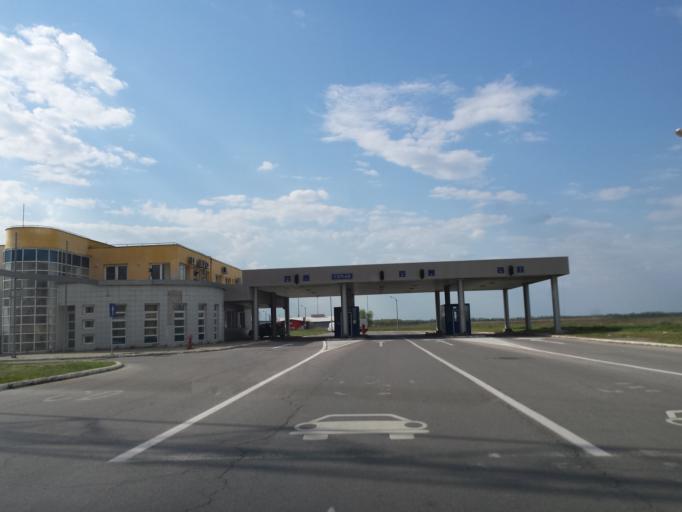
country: HU
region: Csongrad
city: Kiszombor
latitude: 46.1505
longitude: 20.4765
